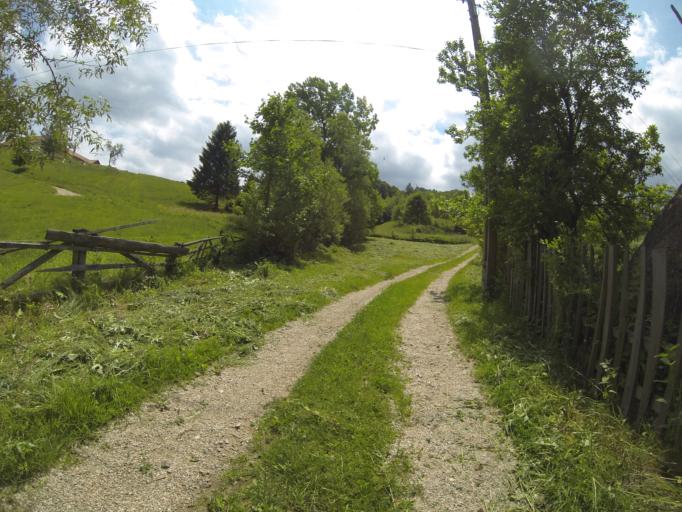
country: RO
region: Brasov
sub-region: Comuna Poiana Marului
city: Poiana Marului
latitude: 45.6554
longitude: 25.2860
